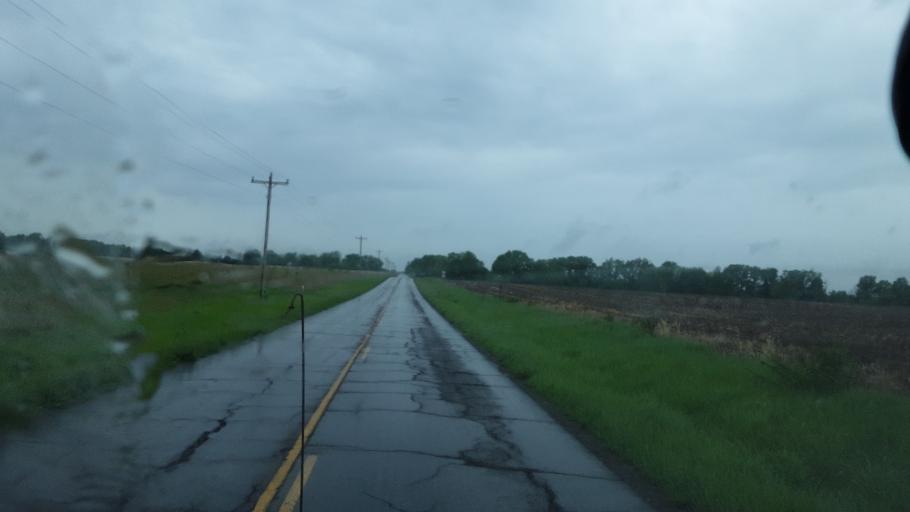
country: US
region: Missouri
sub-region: Randolph County
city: Moberly
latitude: 39.3930
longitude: -92.2428
